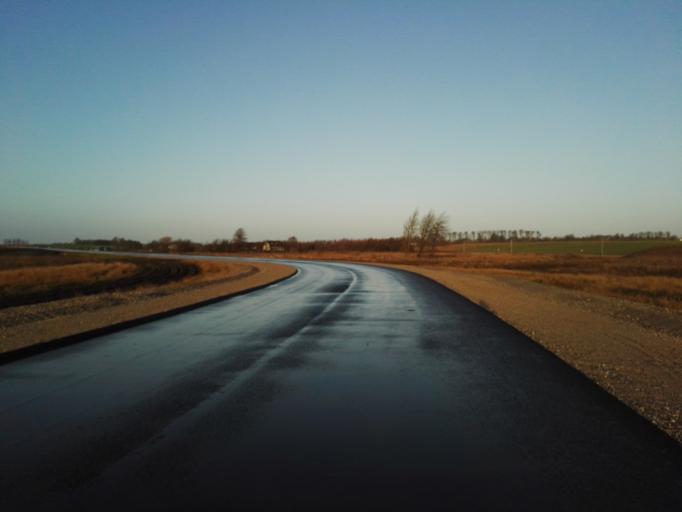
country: DK
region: Capital Region
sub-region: Frederikssund Kommune
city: Frederikssund
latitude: 55.8107
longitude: 12.0990
